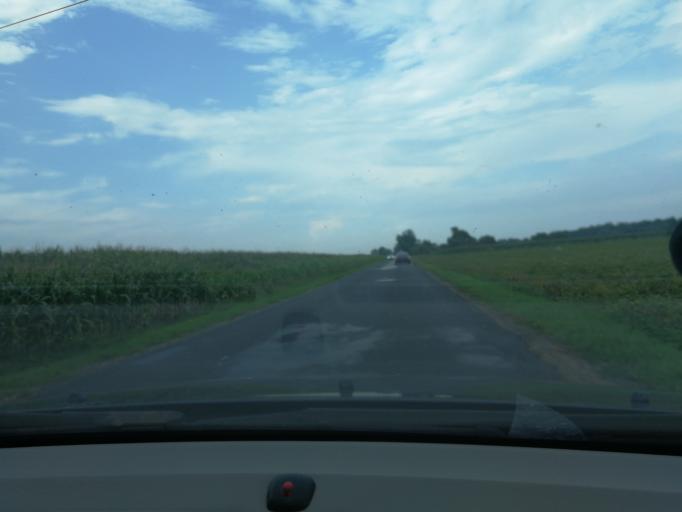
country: PL
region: Masovian Voivodeship
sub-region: Powiat grodziski
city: Grodzisk Mazowiecki
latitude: 52.1248
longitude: 20.5831
